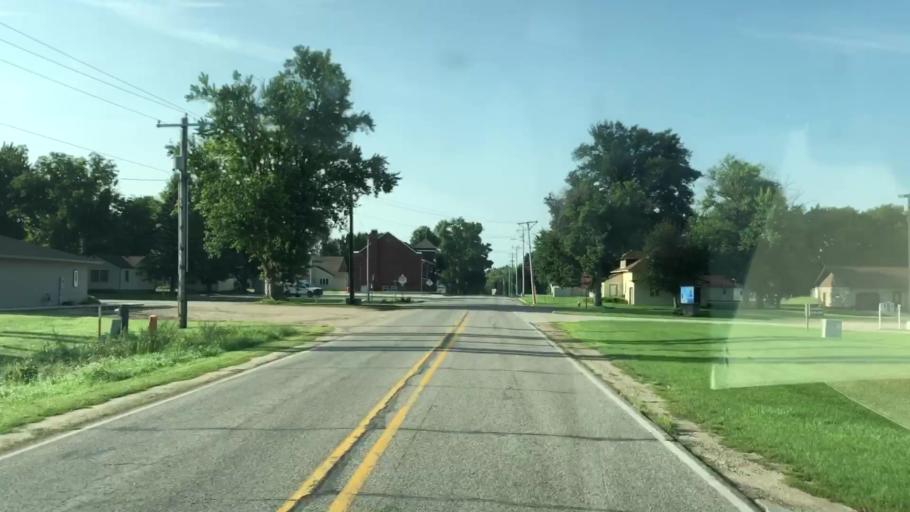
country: US
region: Iowa
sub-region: Lyon County
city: George
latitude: 43.3465
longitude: -95.9984
